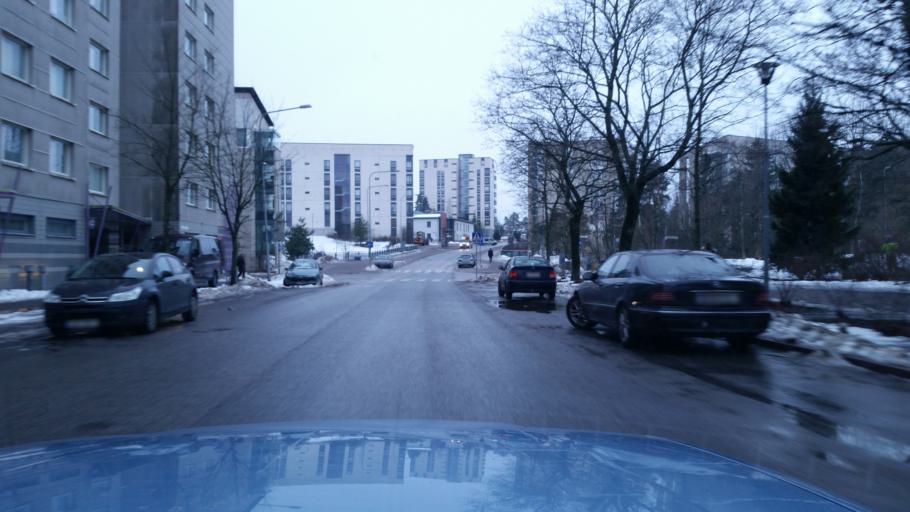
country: FI
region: Uusimaa
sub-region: Helsinki
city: Vantaa
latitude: 60.2308
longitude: 24.9998
